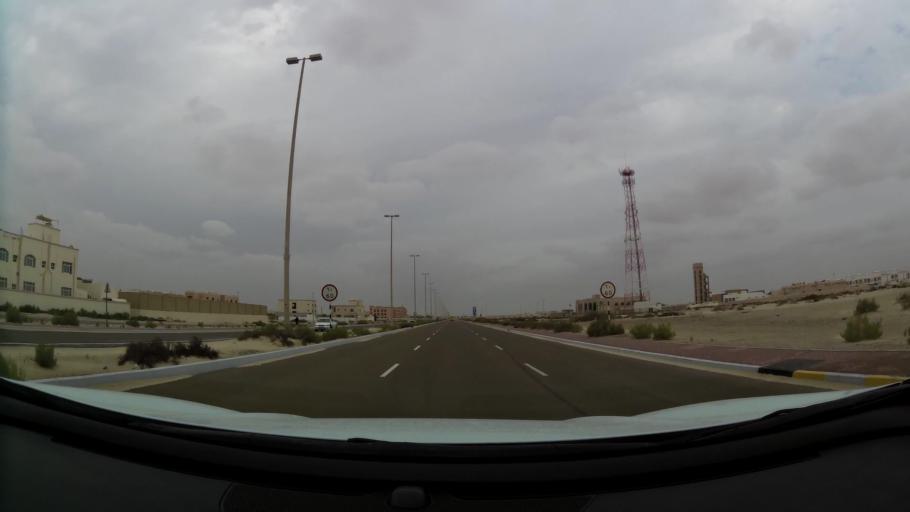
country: AE
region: Abu Dhabi
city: Abu Dhabi
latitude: 24.3584
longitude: 54.6387
